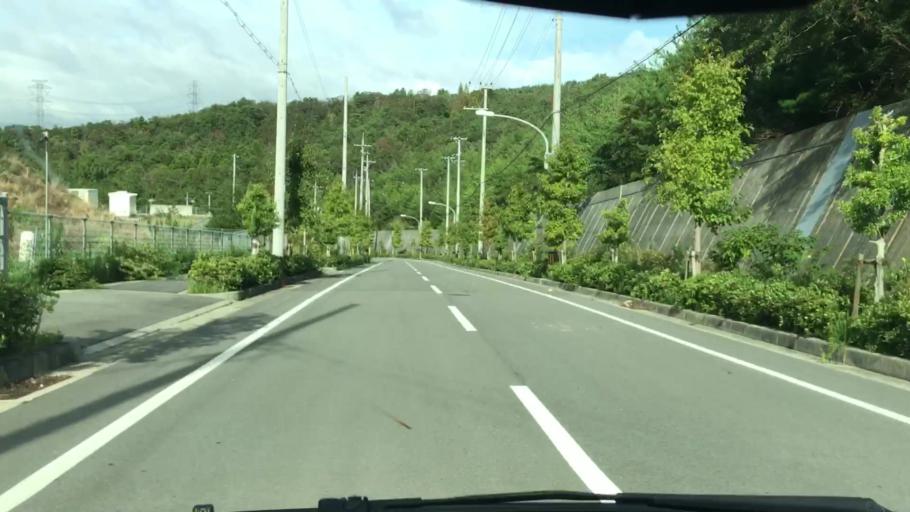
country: JP
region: Hyogo
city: Takarazuka
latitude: 34.8389
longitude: 135.3012
